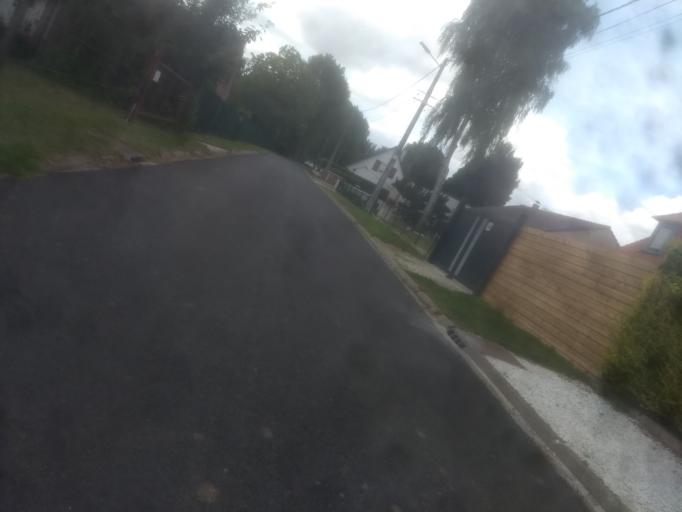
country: FR
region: Nord-Pas-de-Calais
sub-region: Departement du Pas-de-Calais
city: Beaumetz-les-Loges
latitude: 50.2257
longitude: 2.6473
